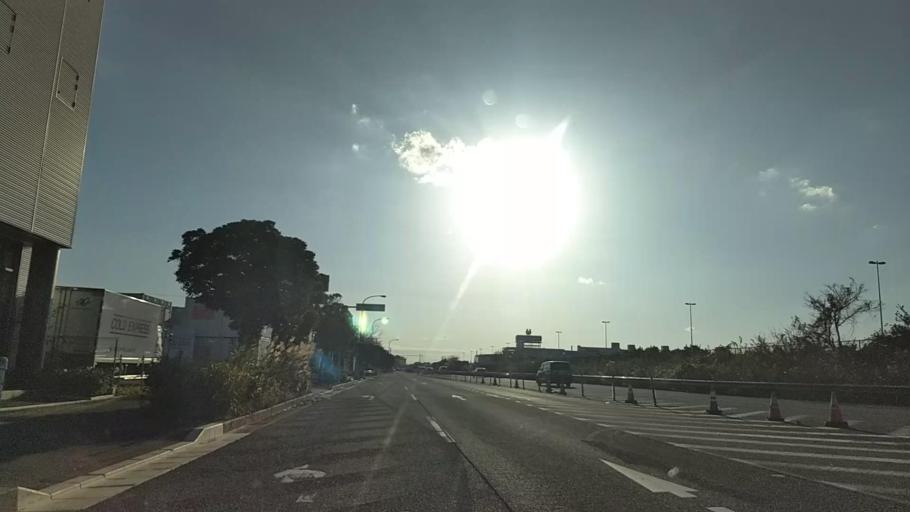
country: JP
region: Tokyo
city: Urayasu
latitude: 35.6676
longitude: 139.9228
